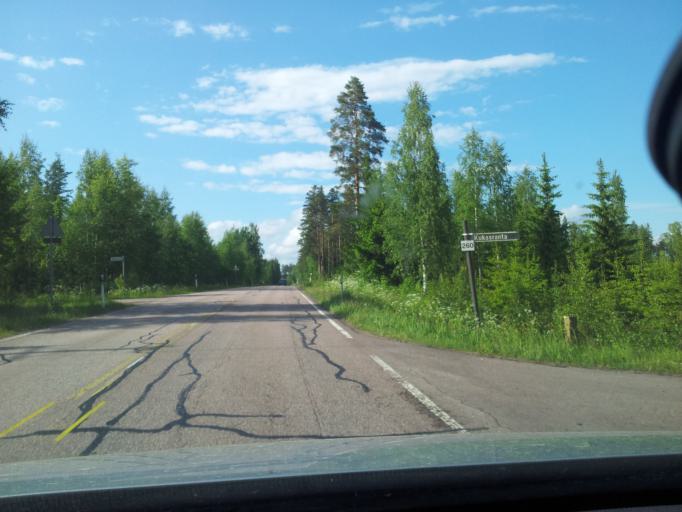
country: FI
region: South Karelia
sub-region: Lappeenranta
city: Luumaeki
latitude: 60.9520
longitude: 27.5788
